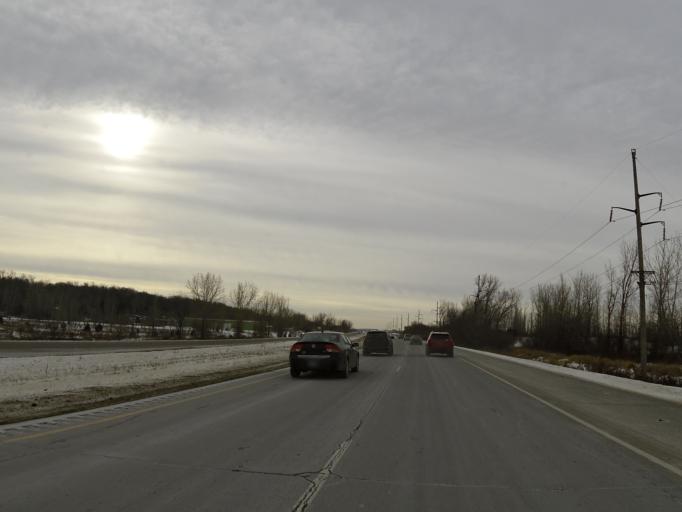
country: US
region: Minnesota
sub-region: Carver County
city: Chaska
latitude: 44.7542
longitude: -93.5861
